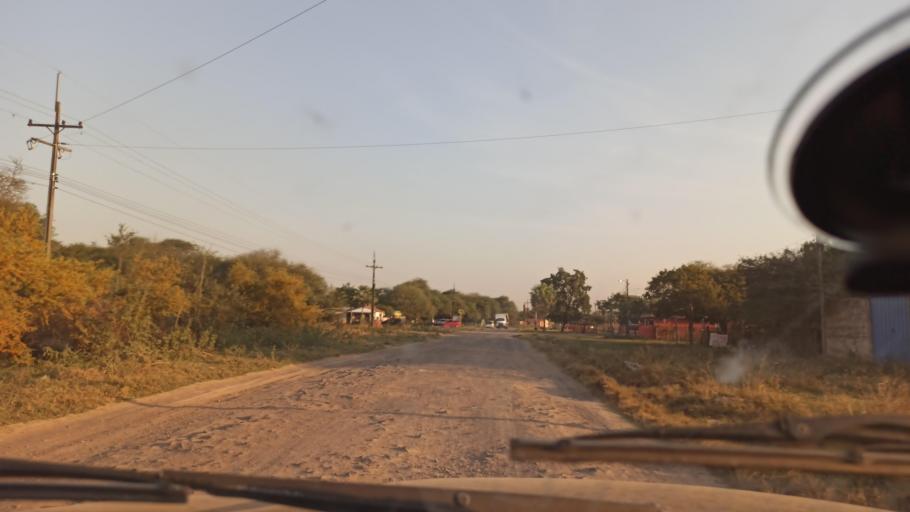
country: PY
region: Presidente Hayes
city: Nanawa
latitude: -25.2328
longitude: -57.6313
